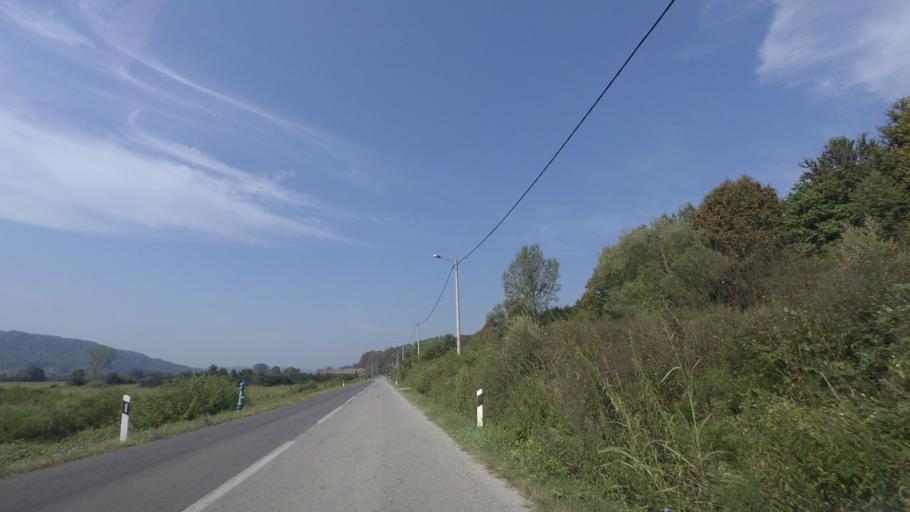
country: HR
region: Sisacko-Moslavacka
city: Hrvatska Kostajnica
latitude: 45.2322
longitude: 16.5908
